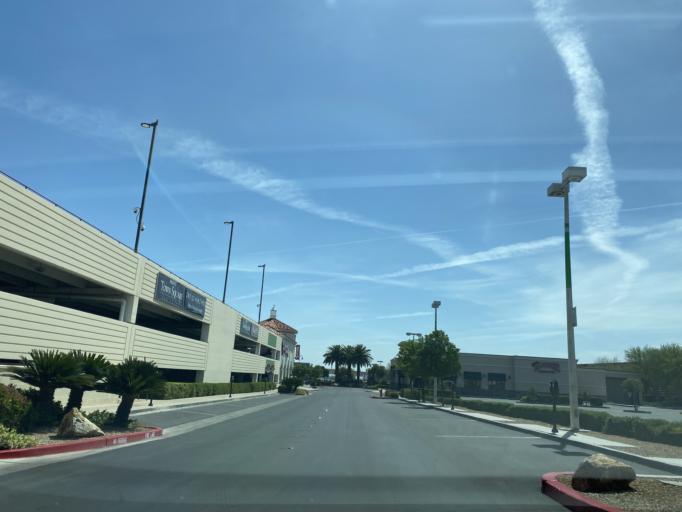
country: US
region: Nevada
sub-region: Clark County
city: Paradise
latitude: 36.0664
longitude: -115.1764
